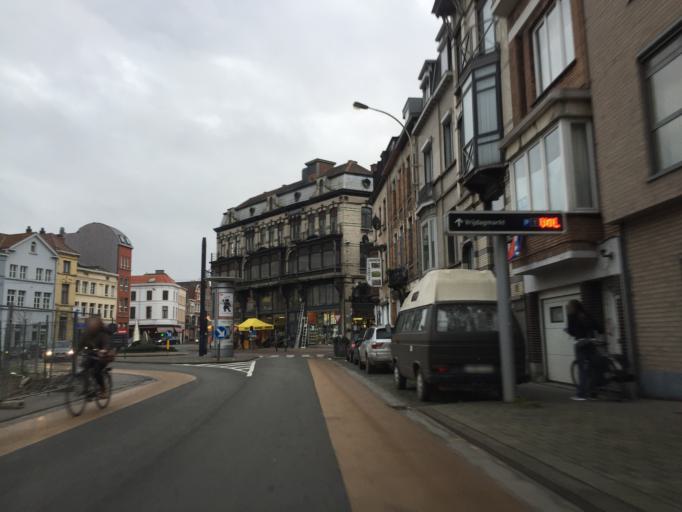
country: BE
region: Flanders
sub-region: Provincie Oost-Vlaanderen
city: Gent
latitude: 51.0605
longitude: 3.7246
